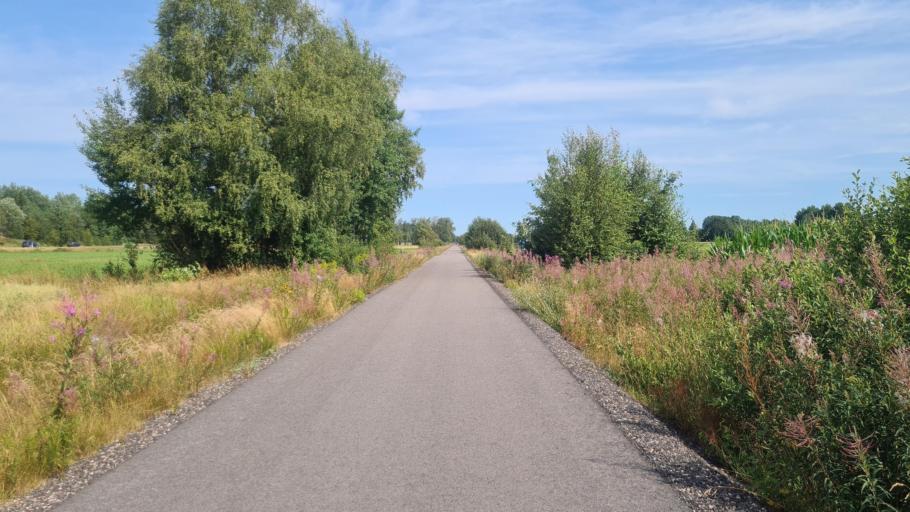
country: SE
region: Kronoberg
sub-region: Ljungby Kommun
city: Lagan
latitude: 56.8757
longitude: 13.9837
